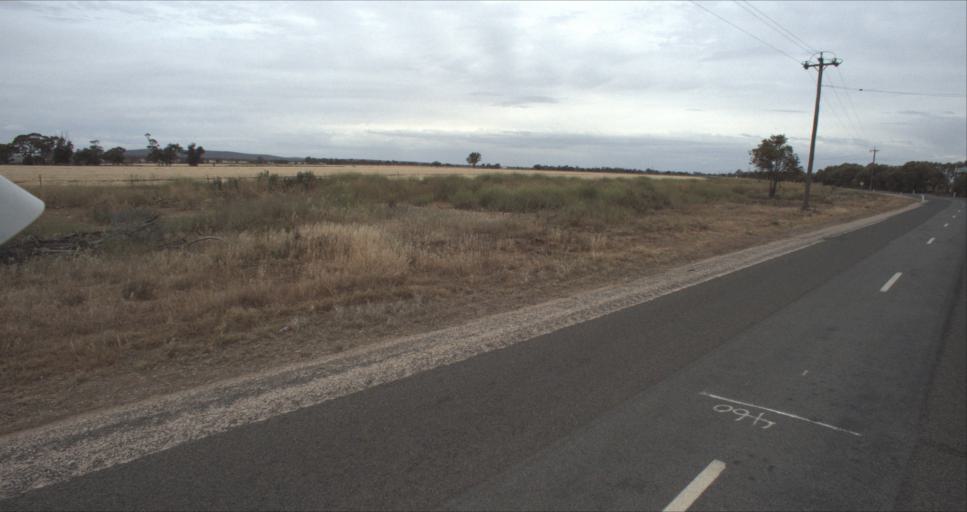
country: AU
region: New South Wales
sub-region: Leeton
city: Leeton
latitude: -34.4745
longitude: 146.3963
